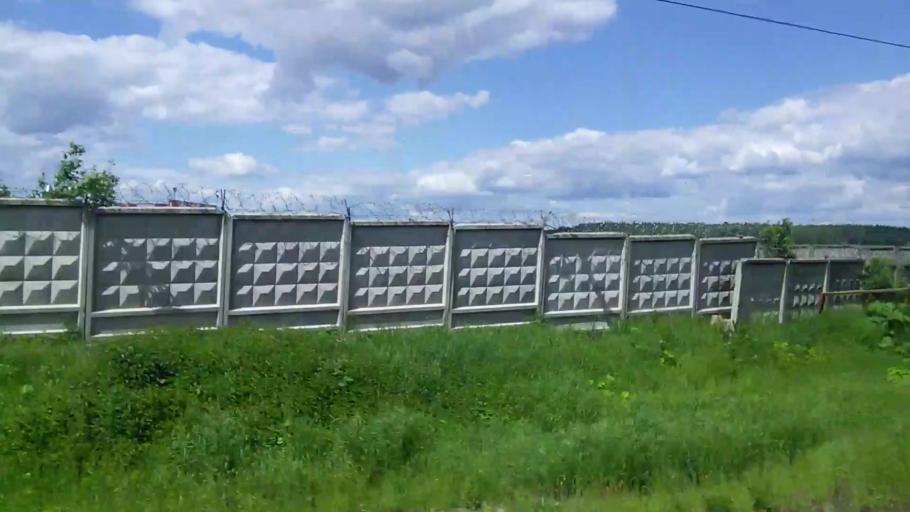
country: RU
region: Moskovskaya
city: Sheremet'yevskiy
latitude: 55.9737
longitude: 37.4505
